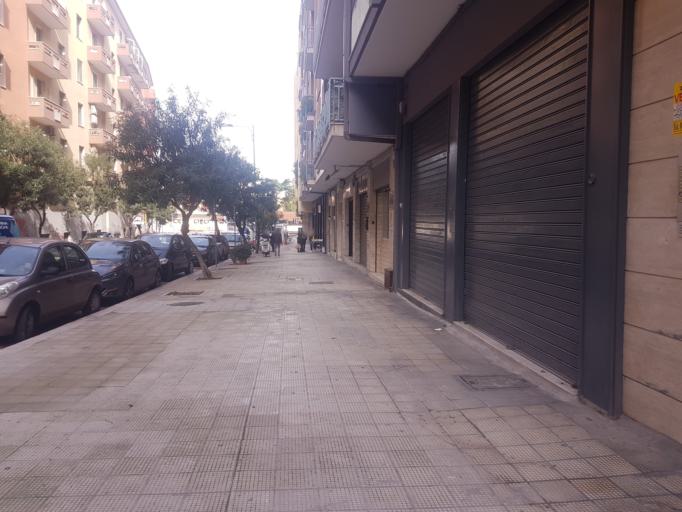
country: IT
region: Apulia
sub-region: Provincia di Bari
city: Bari
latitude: 41.1155
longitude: 16.8624
